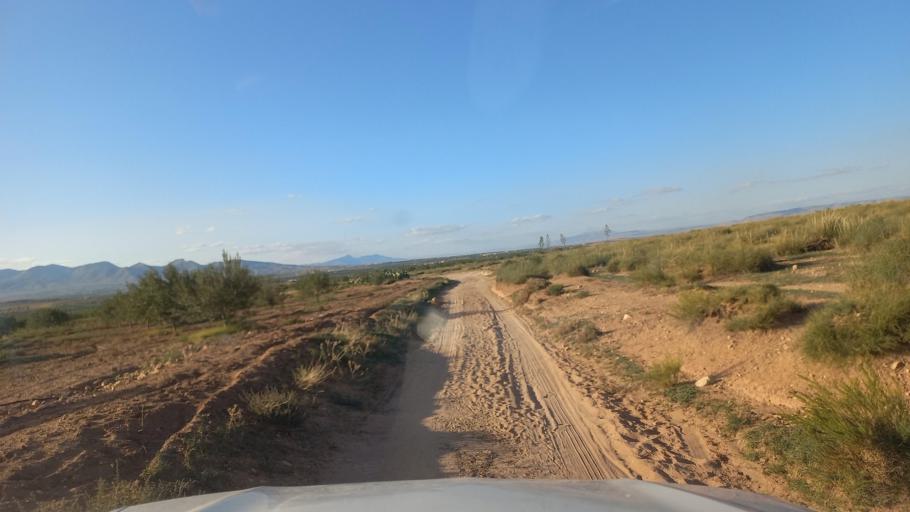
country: TN
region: Al Qasrayn
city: Sbiba
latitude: 35.3872
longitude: 9.1544
